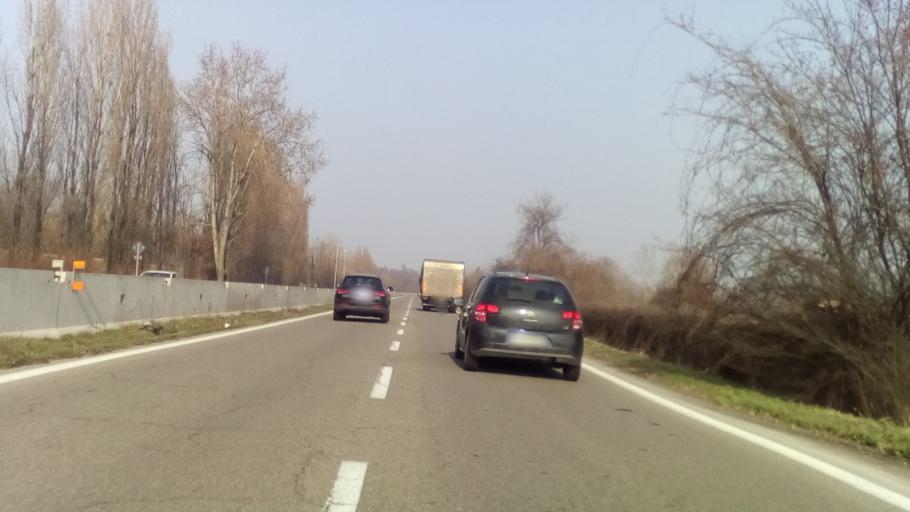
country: IT
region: Emilia-Romagna
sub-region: Provincia di Modena
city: Modena
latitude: 44.6196
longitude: 10.9435
